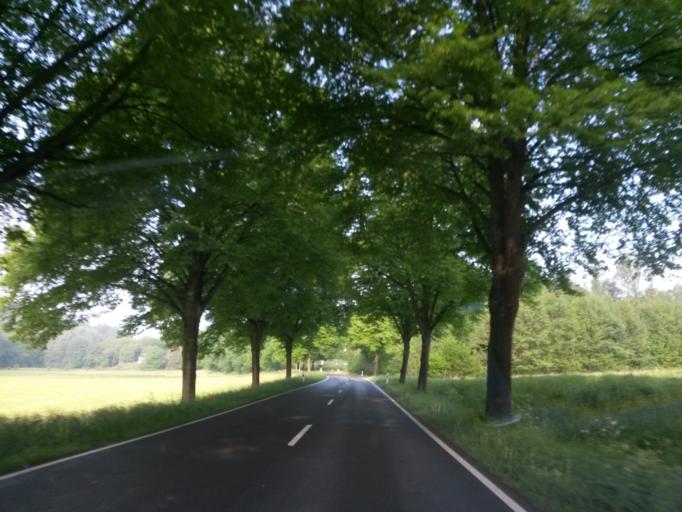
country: DE
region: North Rhine-Westphalia
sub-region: Regierungsbezirk Koln
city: Much
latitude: 50.8830
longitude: 7.3705
